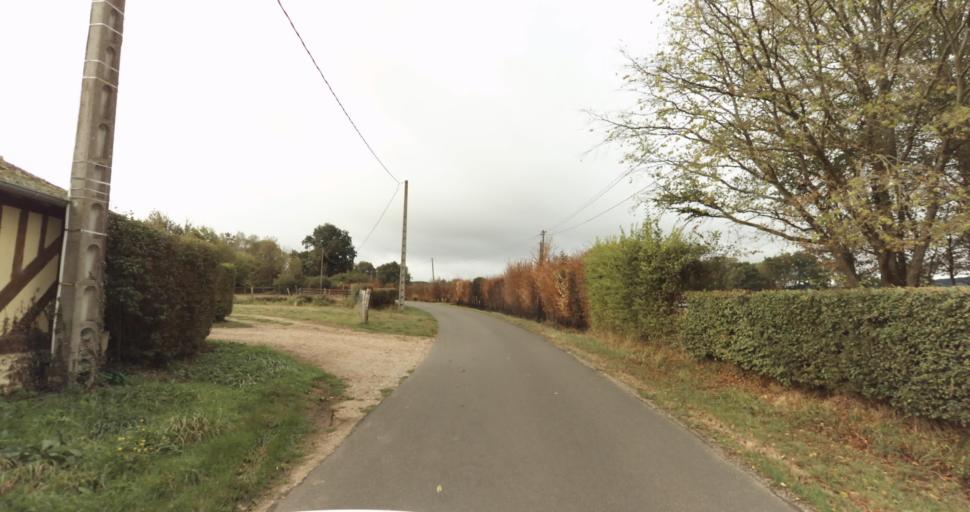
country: FR
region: Lower Normandy
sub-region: Departement du Calvados
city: Livarot
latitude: 48.9344
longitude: 0.1098
